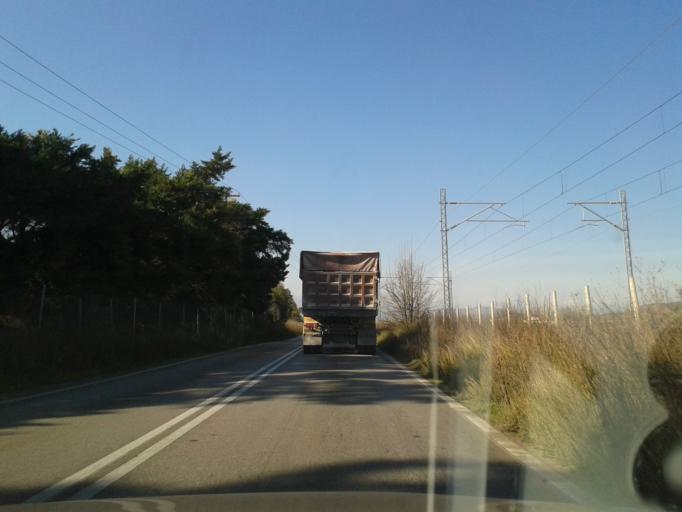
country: GR
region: Central Greece
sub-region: Nomos Voiotias
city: Arma
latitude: 38.3748
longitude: 23.4383
